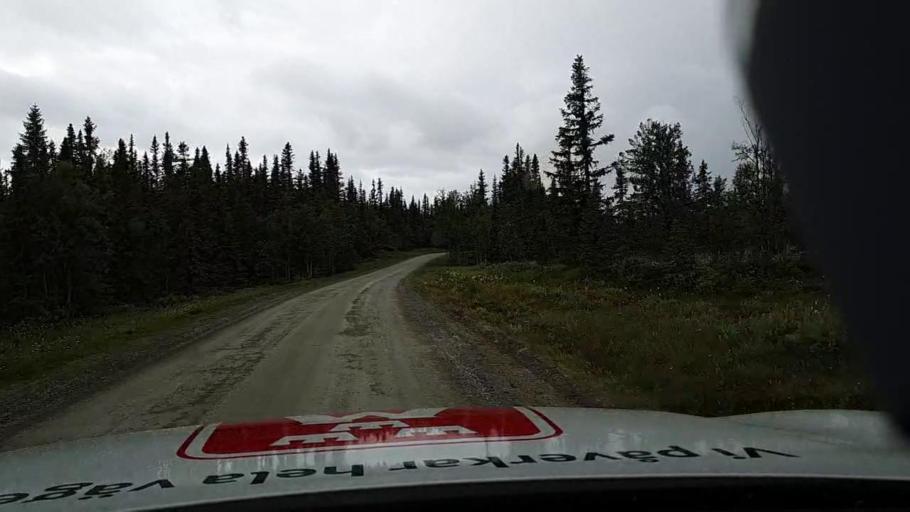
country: SE
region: Jaemtland
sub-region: Bergs Kommun
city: Hoverberg
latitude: 62.8490
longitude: 13.8667
